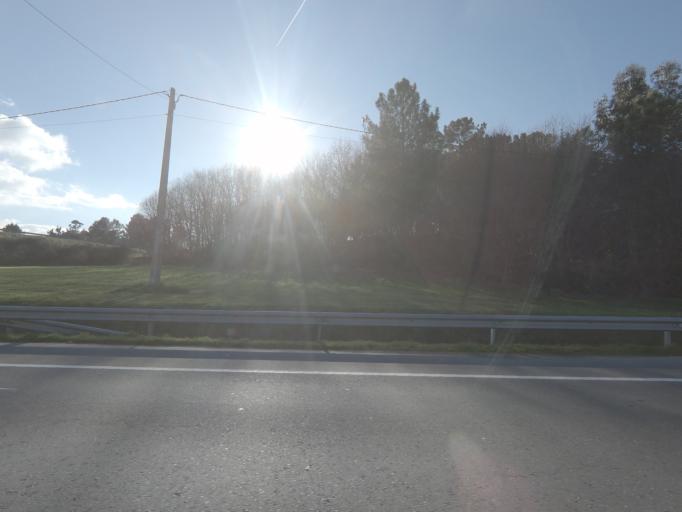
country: ES
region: Galicia
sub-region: Provincia de Pontevedra
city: Silleda
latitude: 42.7200
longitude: -8.2848
